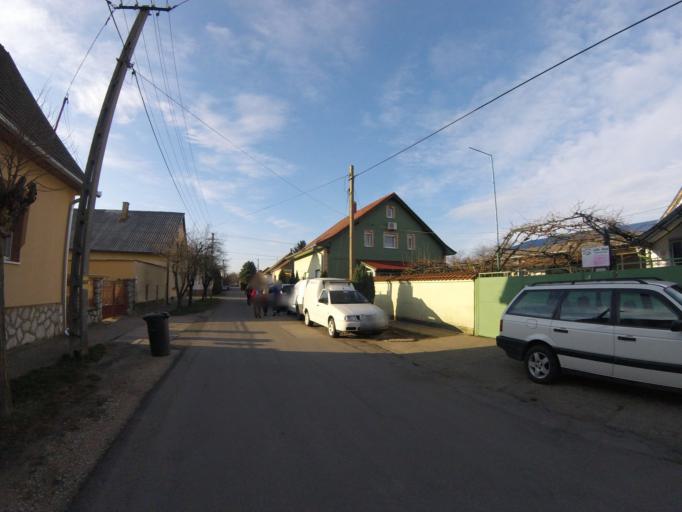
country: HU
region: Baranya
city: Mohacs
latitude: 45.9976
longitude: 18.6762
